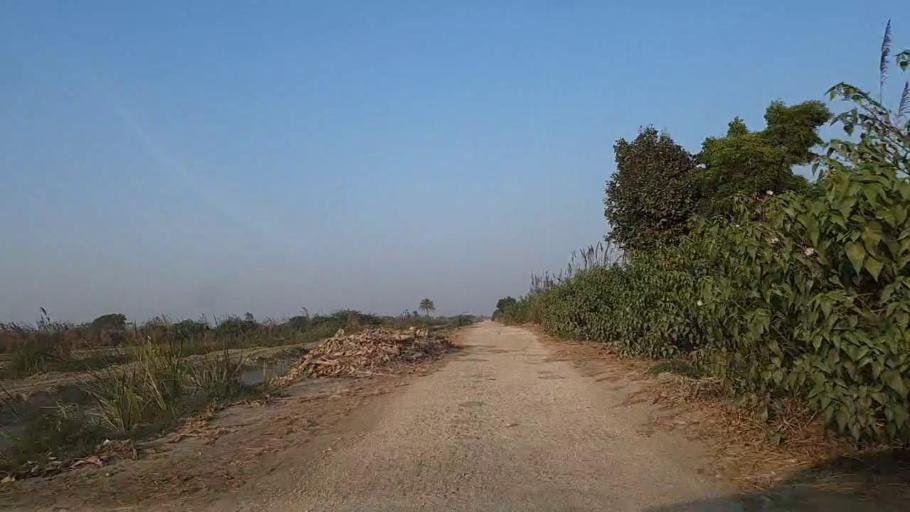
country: PK
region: Sindh
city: Keti Bandar
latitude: 24.2770
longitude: 67.6845
